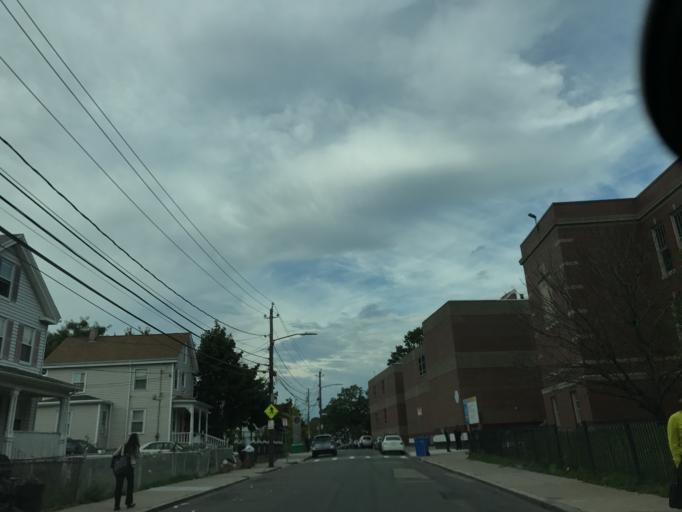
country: US
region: Massachusetts
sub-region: Suffolk County
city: South Boston
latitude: 42.3007
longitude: -71.0609
